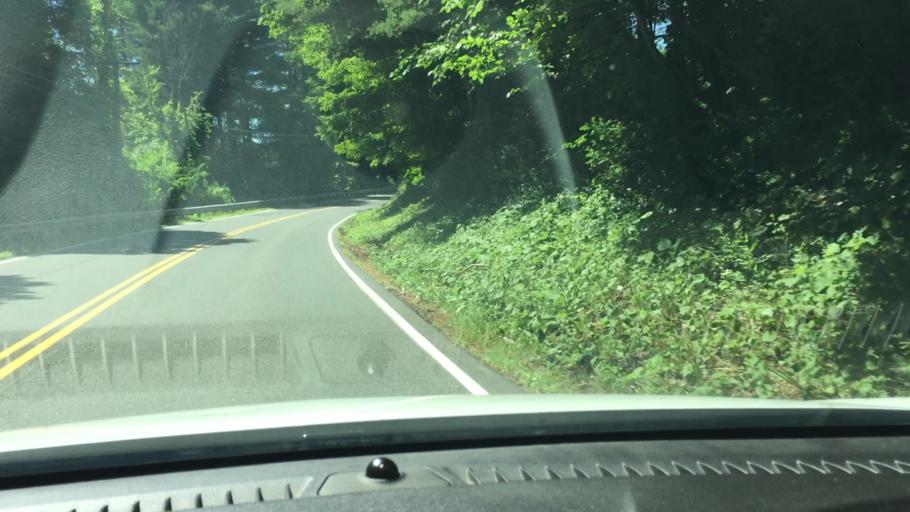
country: US
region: Massachusetts
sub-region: Berkshire County
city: Lenox
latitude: 42.3763
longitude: -73.2573
